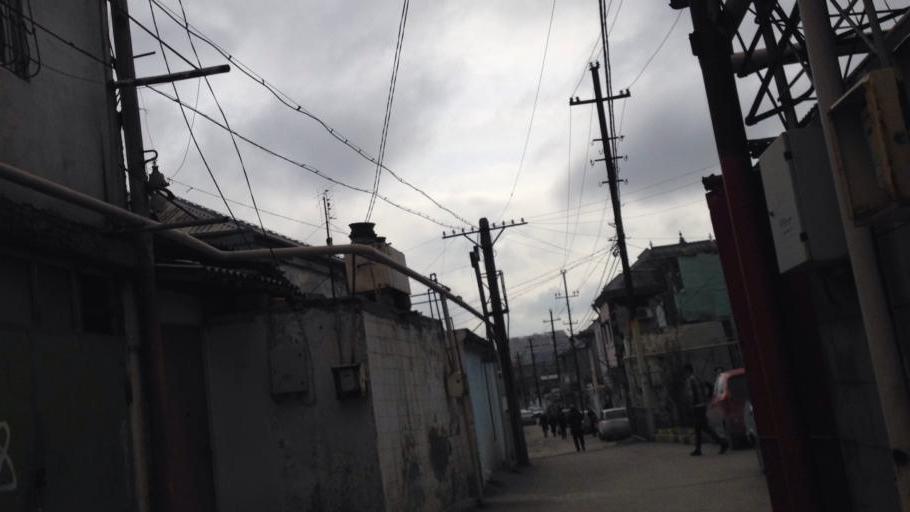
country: AZ
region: Baki
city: Bilajari
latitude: 40.4055
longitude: 49.8262
